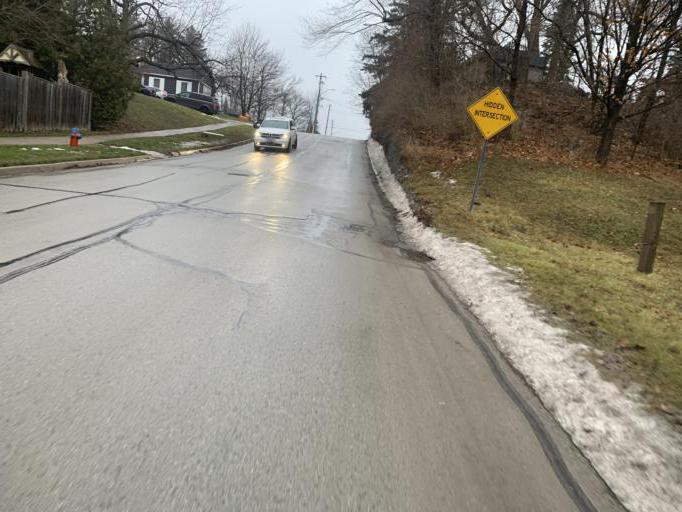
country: CA
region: Ontario
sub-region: Halton
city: Milton
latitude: 43.6583
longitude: -79.9282
